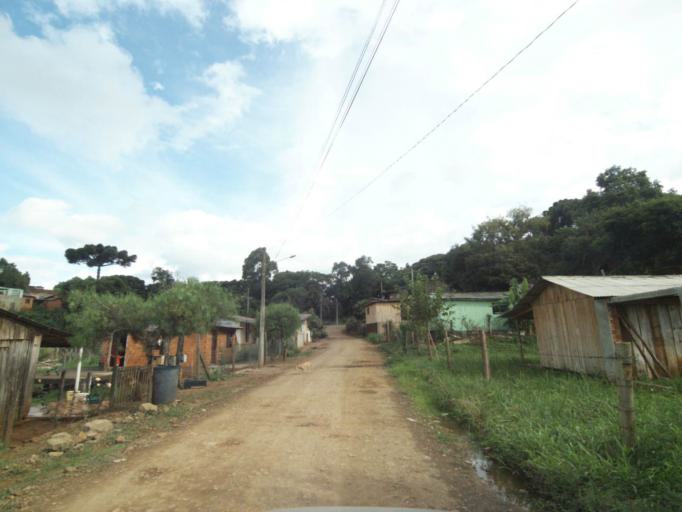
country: BR
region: Rio Grande do Sul
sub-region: Lagoa Vermelha
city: Lagoa Vermelha
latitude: -28.2078
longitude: -51.5363
